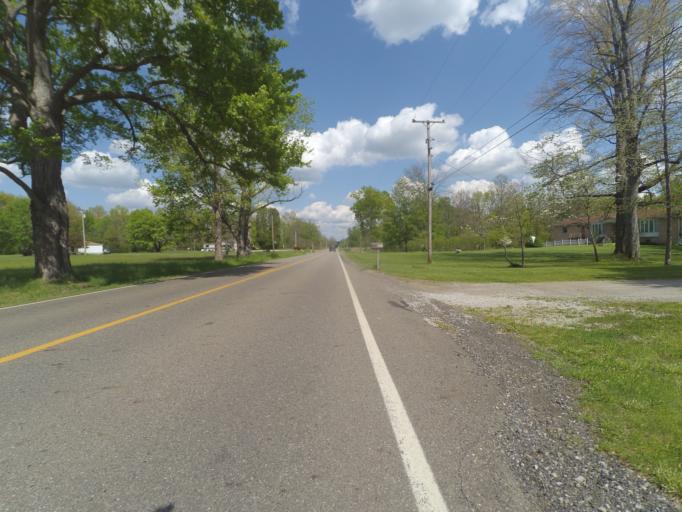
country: US
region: Ohio
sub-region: Trumbull County
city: Lordstown
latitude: 41.1343
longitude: -80.8207
